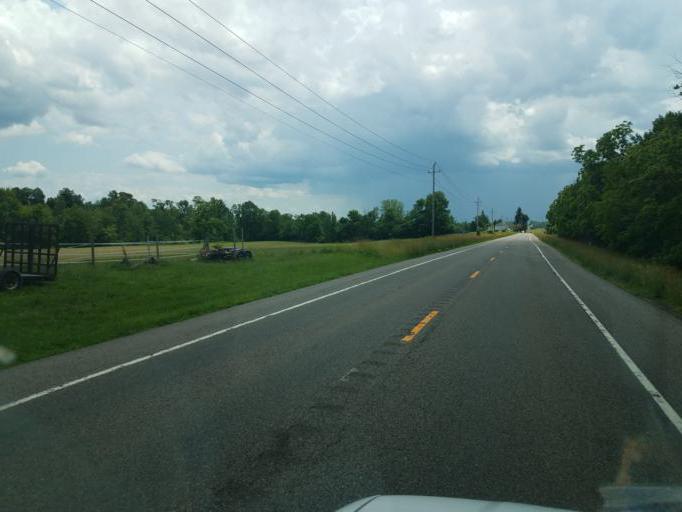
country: US
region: New York
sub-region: Wayne County
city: Clyde
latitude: 42.9987
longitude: -76.8537
